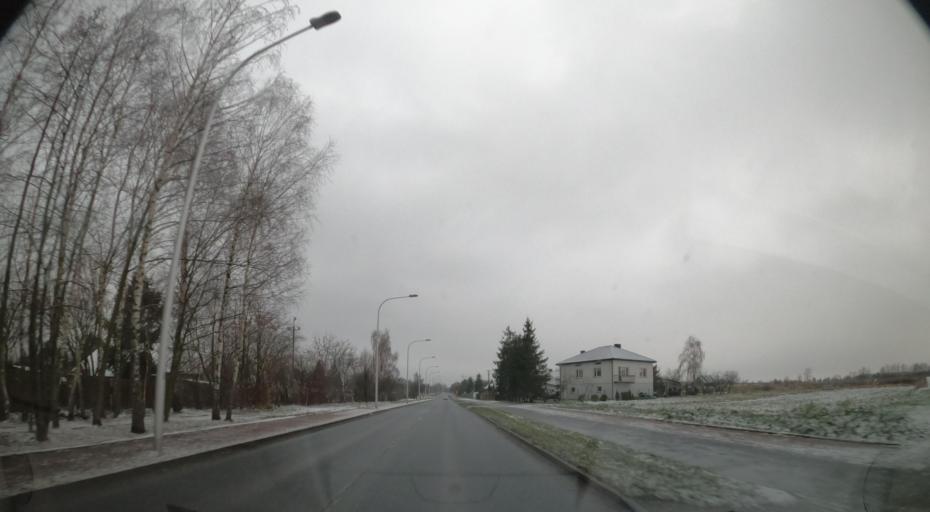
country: PL
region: Masovian Voivodeship
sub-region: Powiat plocki
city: Maszewo Duze
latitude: 52.5636
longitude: 19.6515
